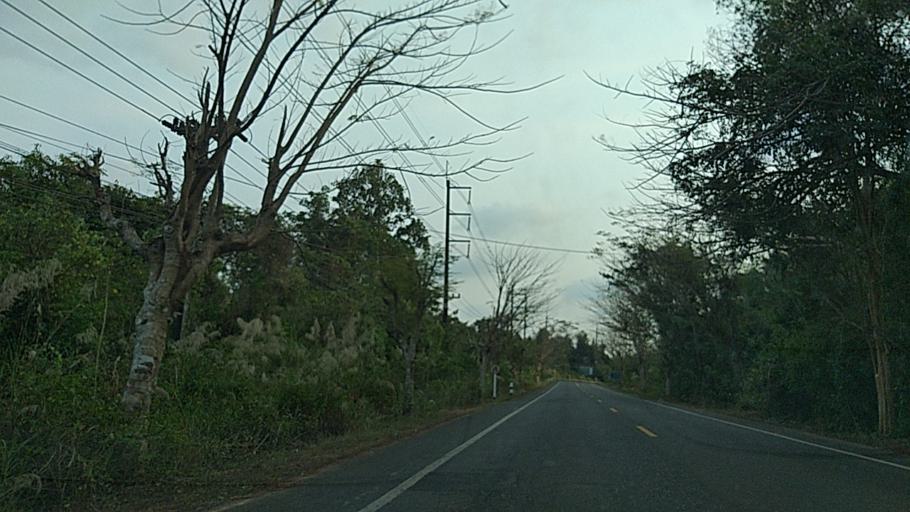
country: TH
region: Trat
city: Laem Ngop
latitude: 12.2682
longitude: 102.3056
